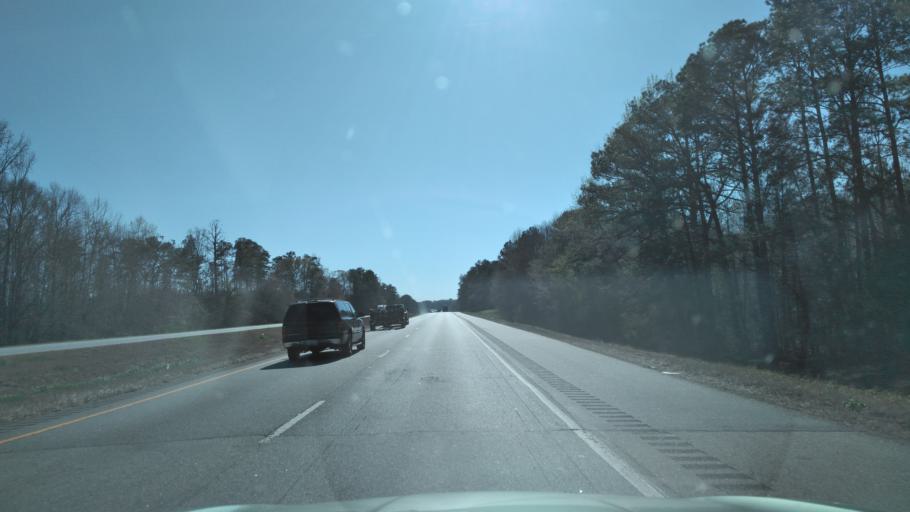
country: US
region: Alabama
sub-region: Lowndes County
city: Fort Deposit
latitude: 31.9581
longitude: -86.5449
